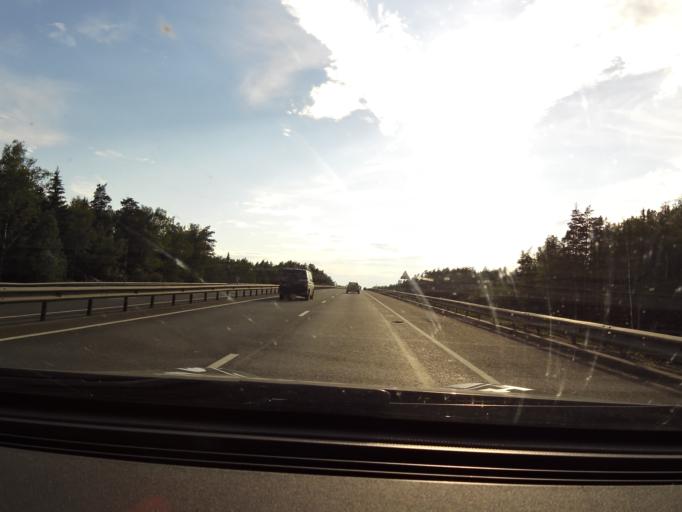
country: RU
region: Vladimir
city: Krasnyy Oktyabr'
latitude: 56.2180
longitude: 41.4521
